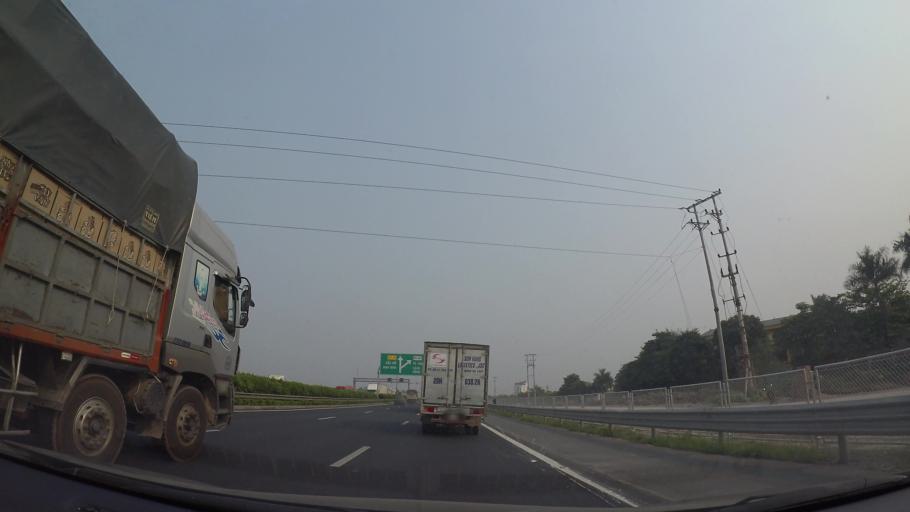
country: VN
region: Ha Noi
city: Thuong Tin
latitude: 20.8753
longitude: 105.8763
